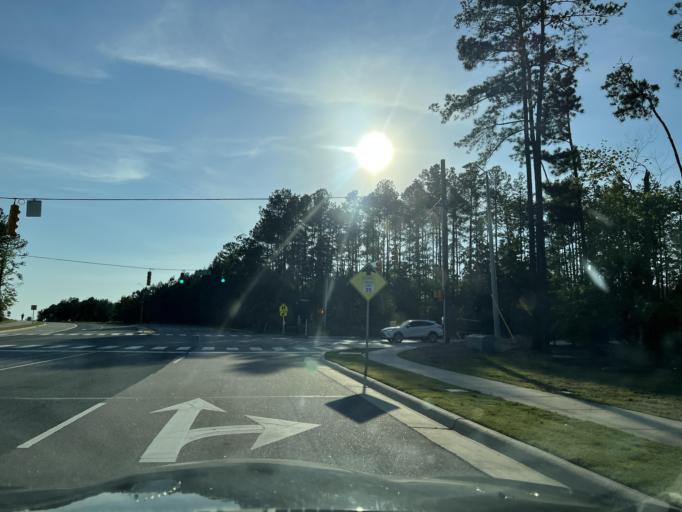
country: US
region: North Carolina
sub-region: Wake County
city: Green Level
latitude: 35.8293
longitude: -78.8837
